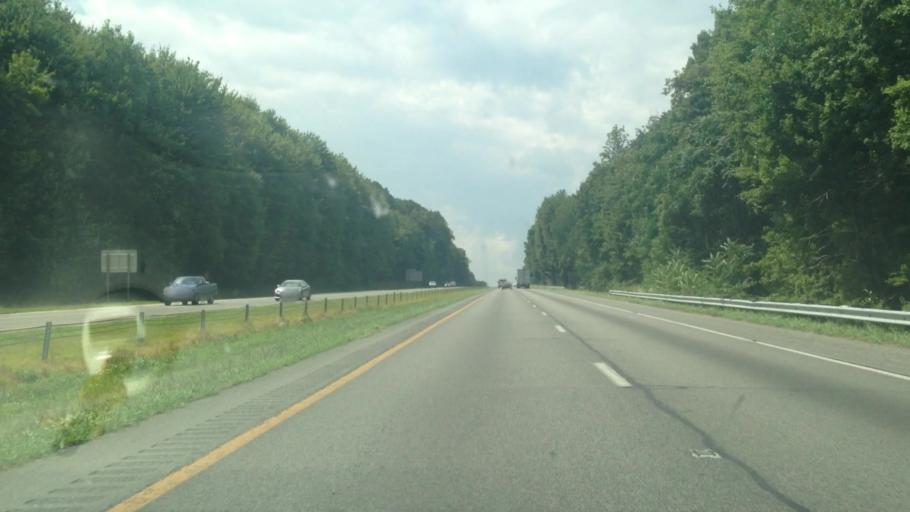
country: US
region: North Carolina
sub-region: Surry County
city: Pilot Mountain
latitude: 36.3443
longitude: -80.4615
